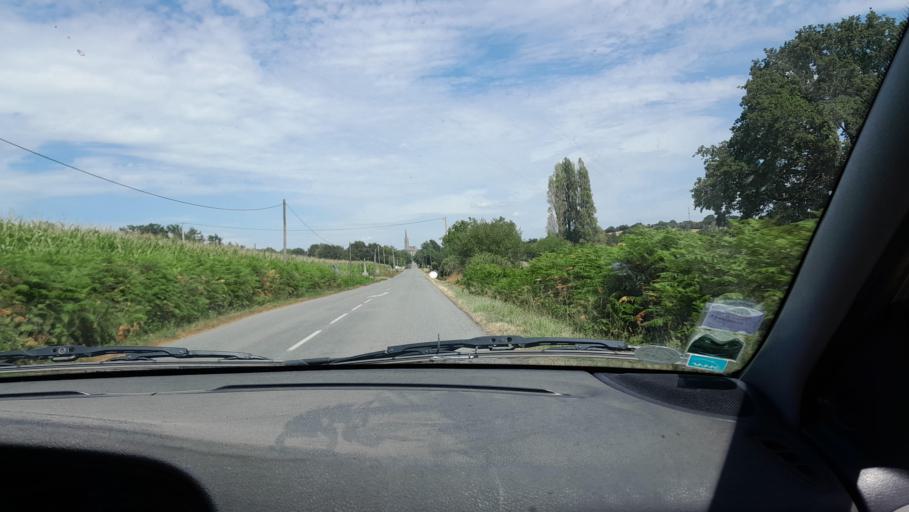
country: FR
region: Brittany
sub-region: Departement d'Ille-et-Vilaine
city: Le Pertre
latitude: 48.0173
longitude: -1.0377
